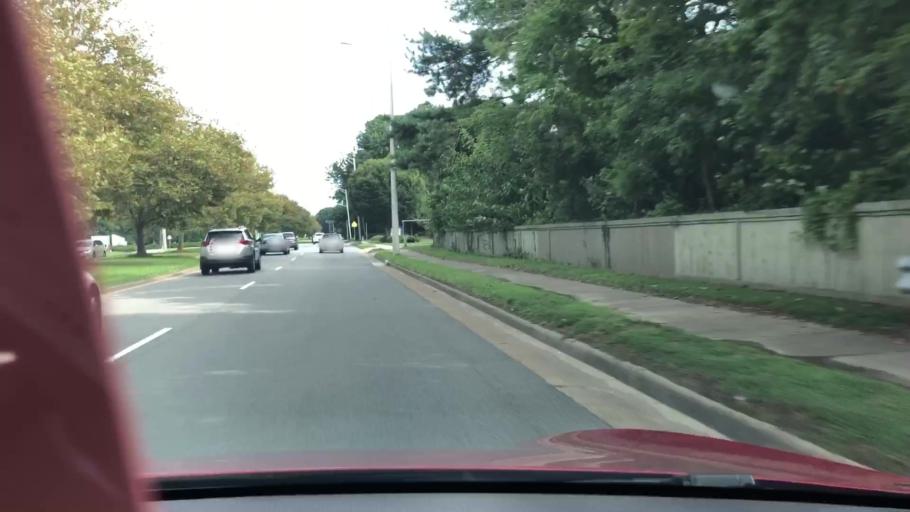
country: US
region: Virginia
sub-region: City of Virginia Beach
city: Virginia Beach
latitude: 36.8972
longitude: -76.0632
